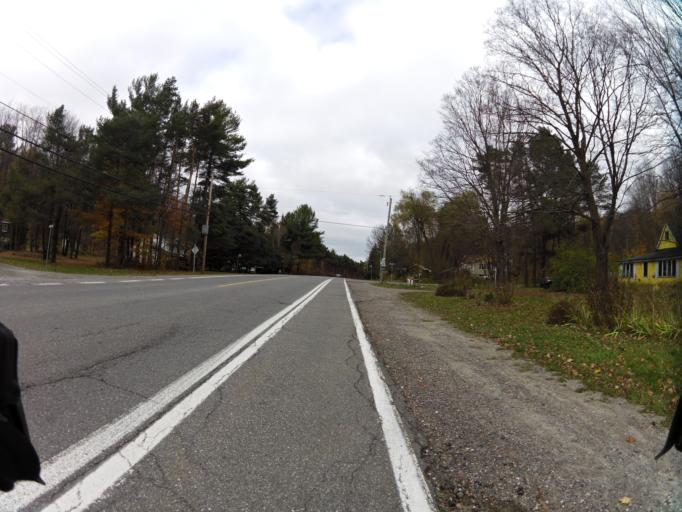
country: CA
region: Quebec
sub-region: Outaouais
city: Gatineau
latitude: 45.5183
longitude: -75.8085
